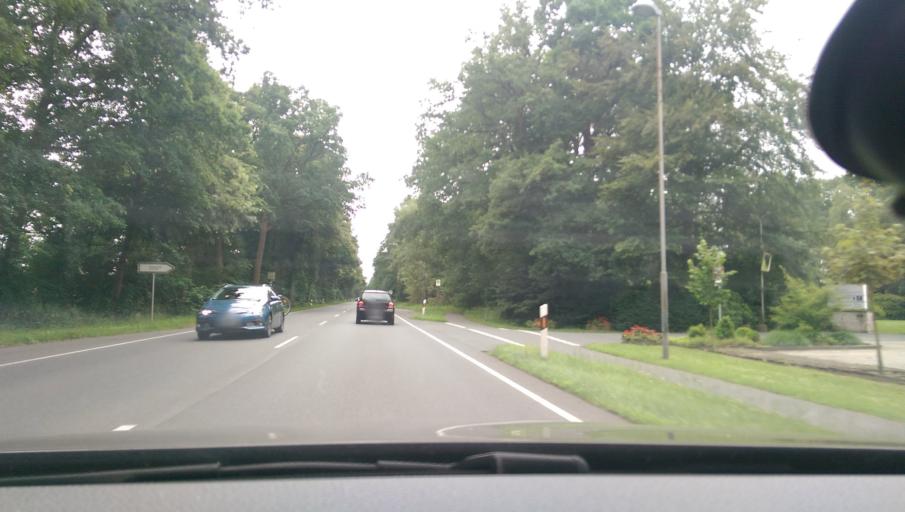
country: DE
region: Lower Saxony
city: Rotenburg
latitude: 53.0900
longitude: 9.3681
